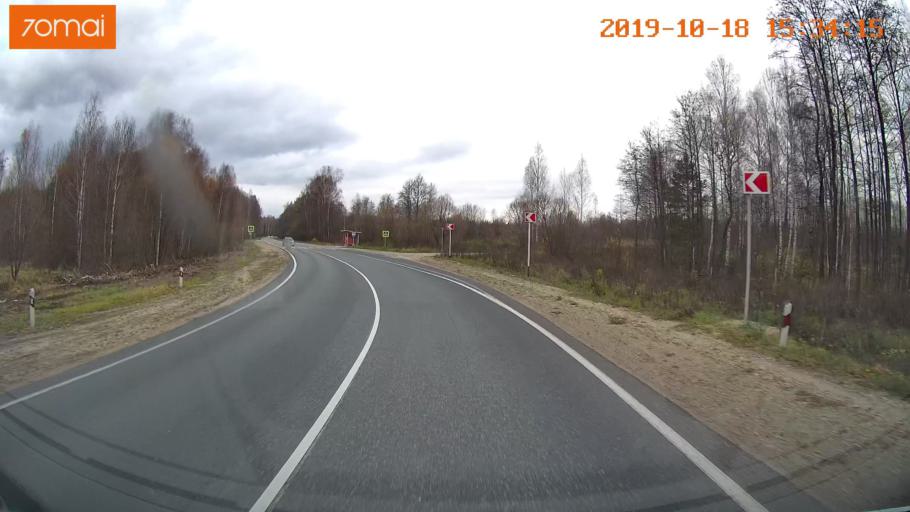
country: RU
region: Vladimir
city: Anopino
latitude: 55.8525
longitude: 40.6447
